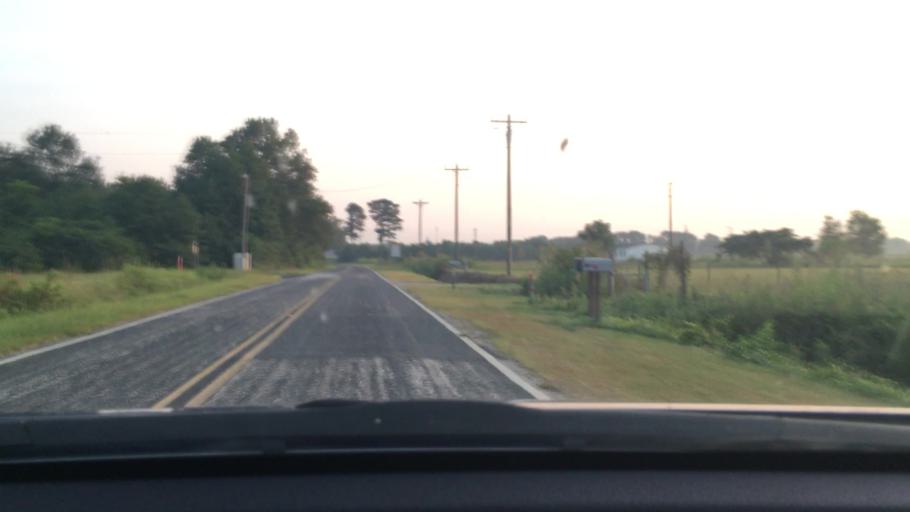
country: US
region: South Carolina
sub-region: Lee County
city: Bishopville
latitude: 34.2440
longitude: -80.1333
